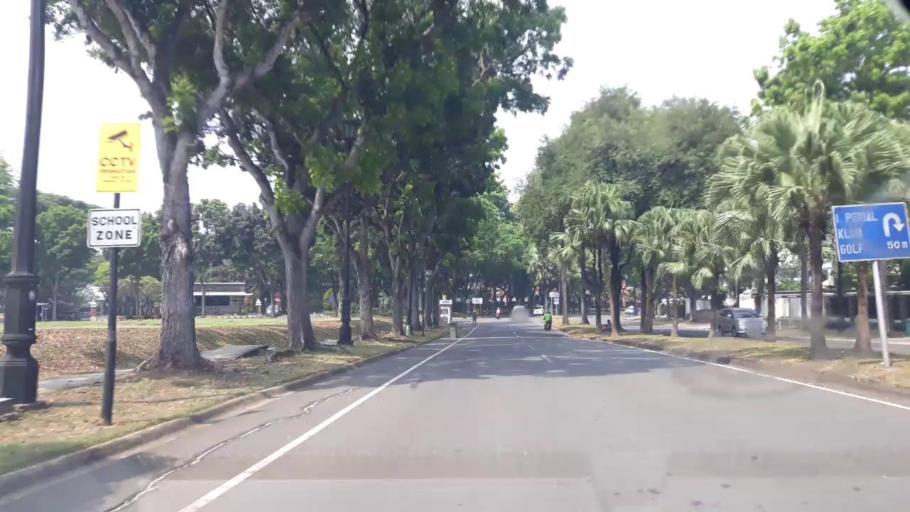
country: ID
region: Banten
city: Curug
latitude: -6.2387
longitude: 106.6076
